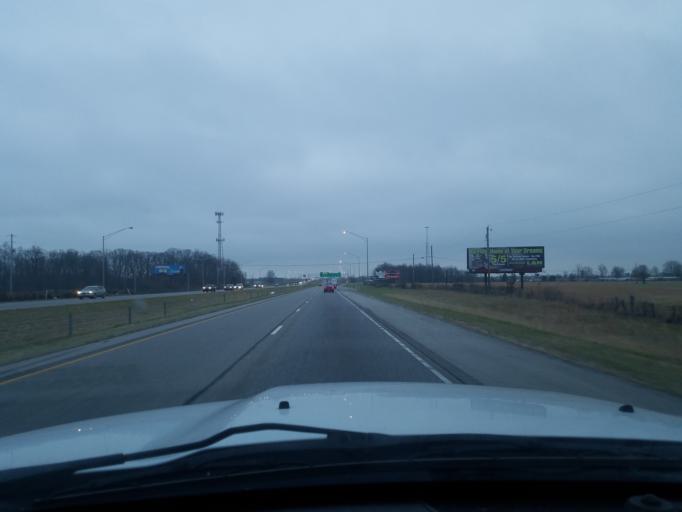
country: US
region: Indiana
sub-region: Clark County
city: Clarksville
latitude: 38.3453
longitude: -85.7651
